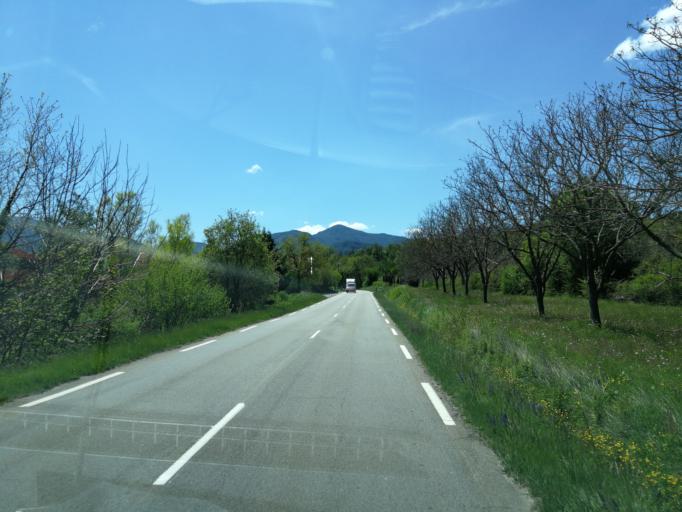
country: FR
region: Rhone-Alpes
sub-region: Departement de la Drome
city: Die
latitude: 44.7301
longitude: 5.2668
